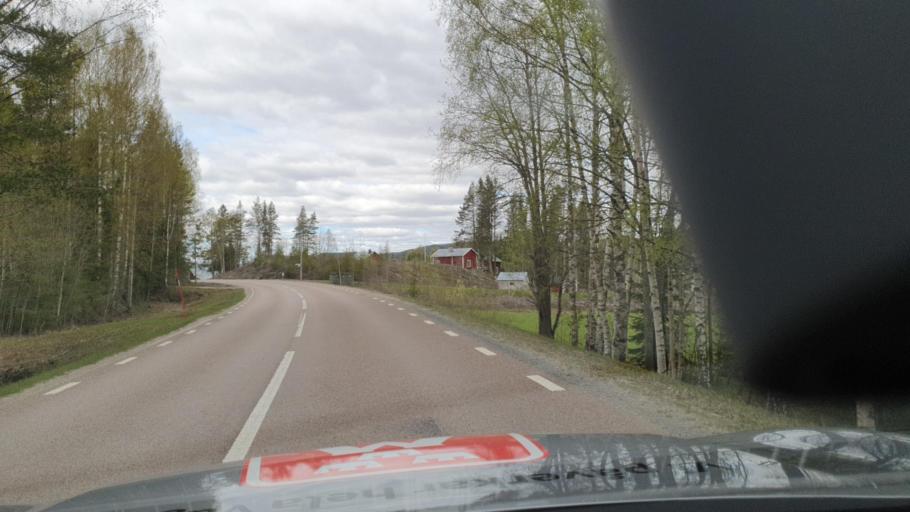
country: SE
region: Vaesternorrland
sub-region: OErnskoeldsviks Kommun
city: Ornskoldsvik
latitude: 63.5032
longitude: 18.8490
